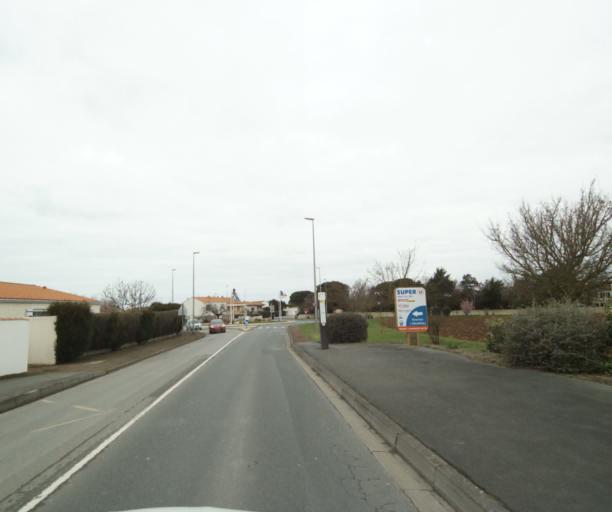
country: FR
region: Poitou-Charentes
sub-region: Departement de la Charente-Maritime
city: Nieul-sur-Mer
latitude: 46.1997
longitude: -1.1598
